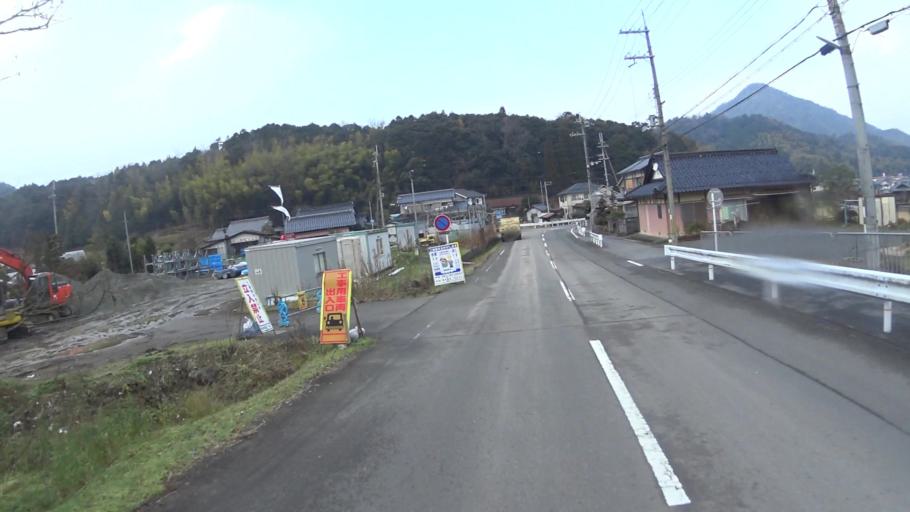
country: JP
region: Kyoto
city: Maizuru
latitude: 35.4408
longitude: 135.2958
